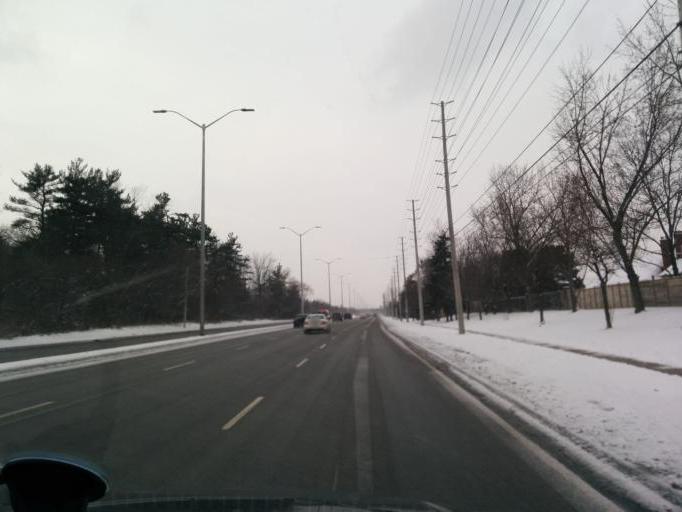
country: CA
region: Ontario
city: Mississauga
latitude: 43.5318
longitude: -79.6585
